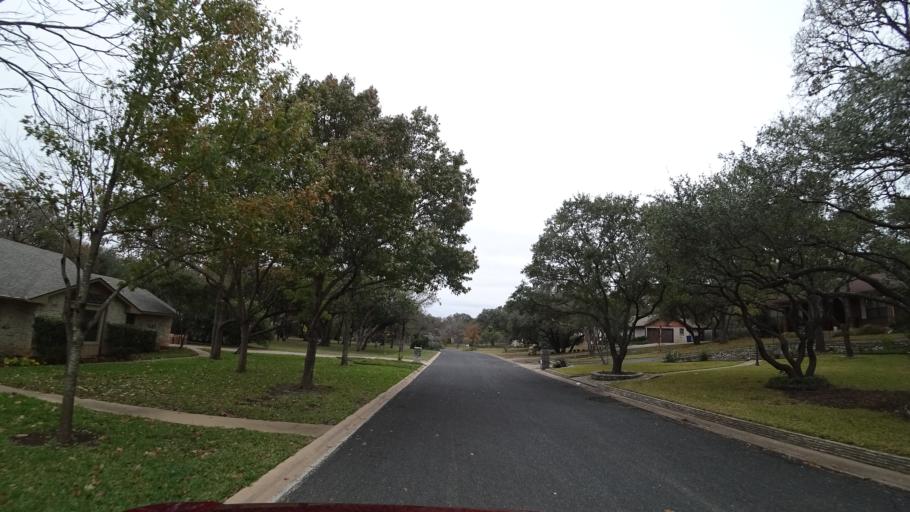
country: US
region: Texas
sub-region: Williamson County
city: Jollyville
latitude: 30.3774
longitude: -97.7850
